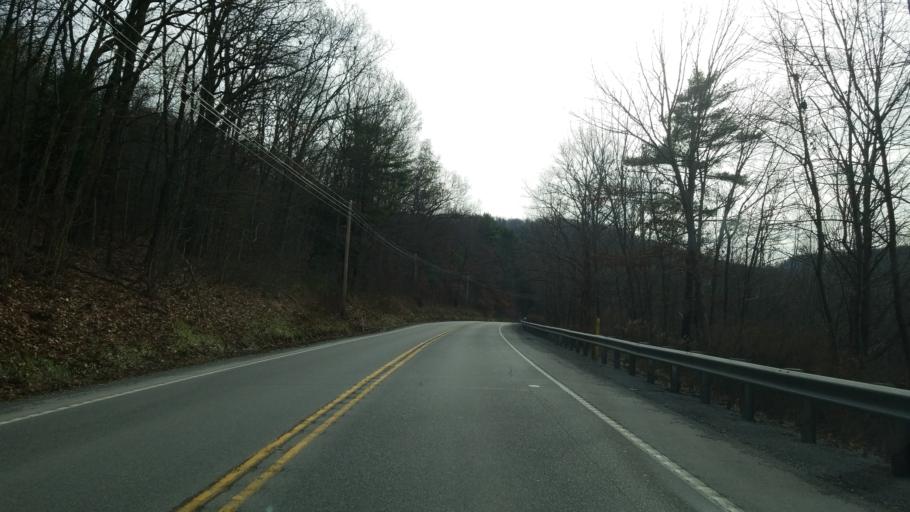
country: US
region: Pennsylvania
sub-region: Clearfield County
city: Clearfield
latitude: 41.0082
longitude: -78.3857
